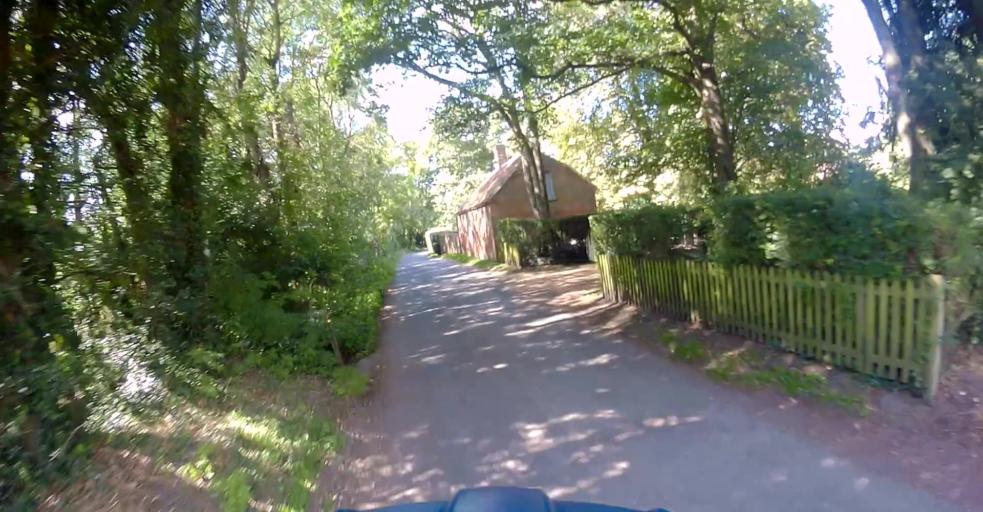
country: GB
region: England
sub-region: Hampshire
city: Four Marks
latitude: 51.1699
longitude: -1.0933
